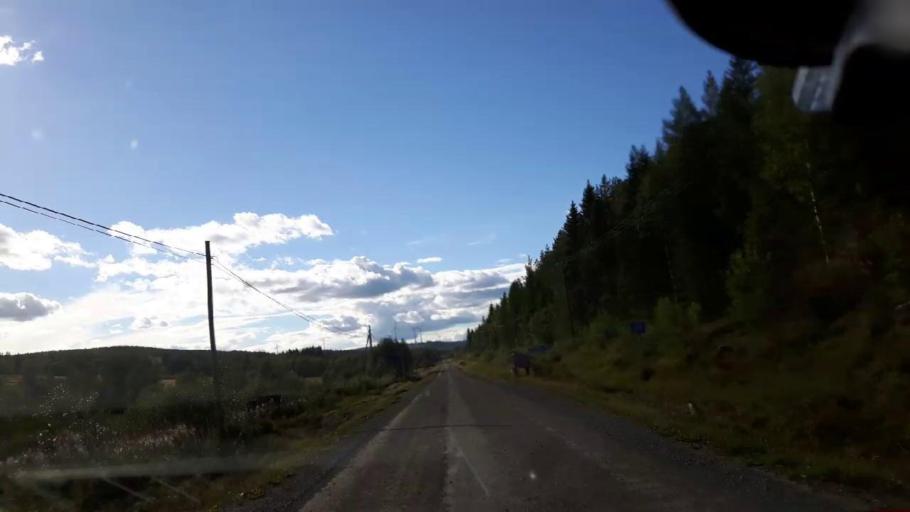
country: SE
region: Jaemtland
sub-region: Ragunda Kommun
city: Hammarstrand
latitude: 63.4882
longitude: 16.0833
